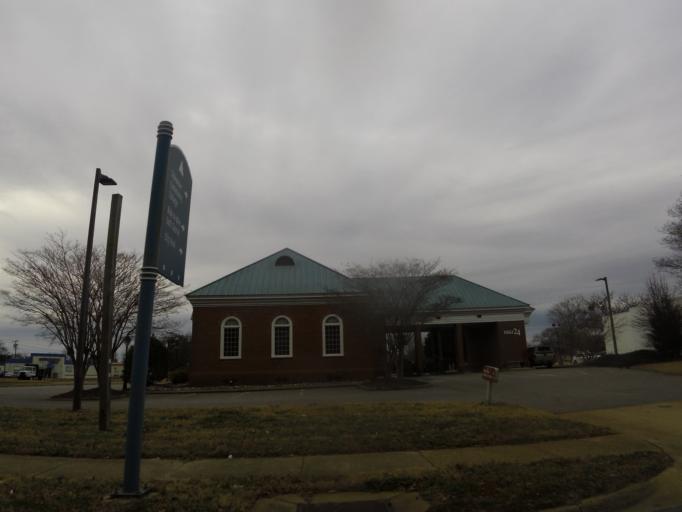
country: US
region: Virginia
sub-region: City of Portsmouth
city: Portsmouth Heights
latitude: 36.8343
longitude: -76.3421
